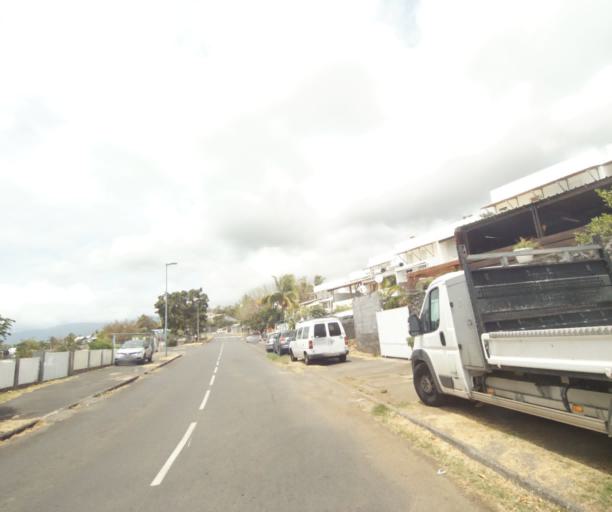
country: RE
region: Reunion
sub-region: Reunion
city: Saint-Paul
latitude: -21.0231
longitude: 55.2699
